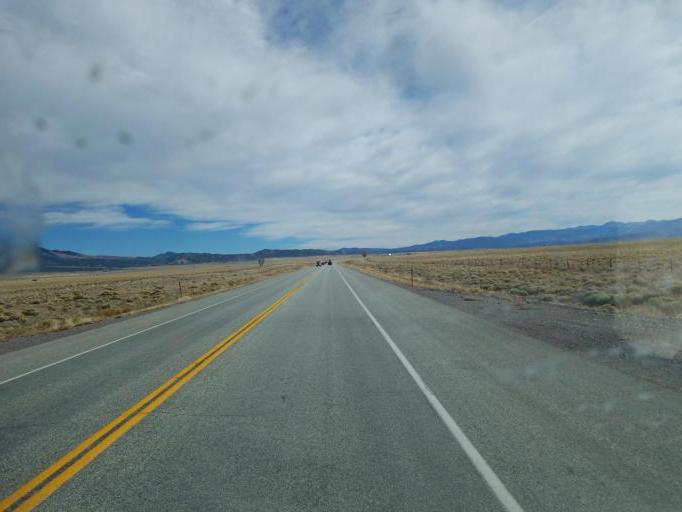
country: US
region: Colorado
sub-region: Alamosa County
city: Alamosa East
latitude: 37.4749
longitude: -105.5946
